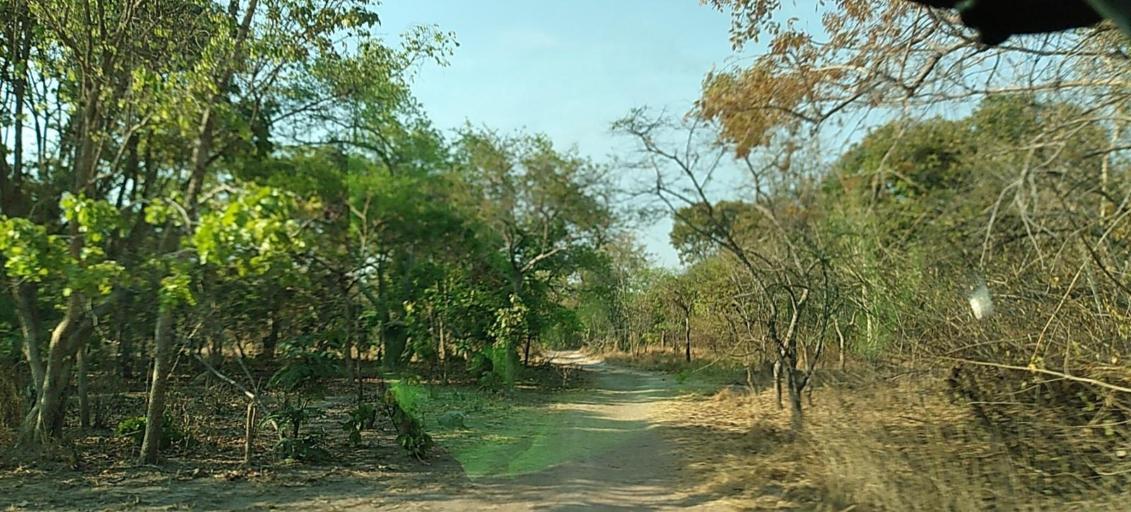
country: ZM
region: North-Western
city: Kalengwa
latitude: -13.1836
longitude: 25.0404
